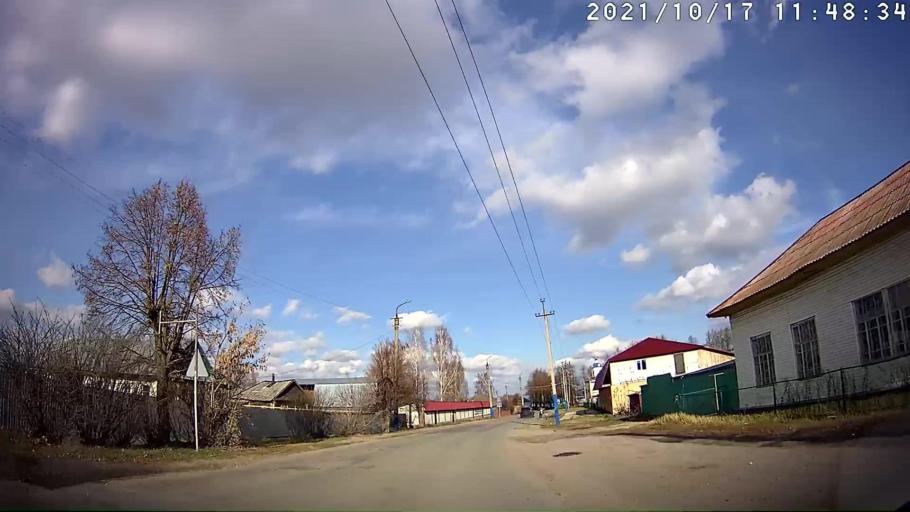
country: RU
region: Mariy-El
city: Kuzhener
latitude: 57.0035
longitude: 48.7340
